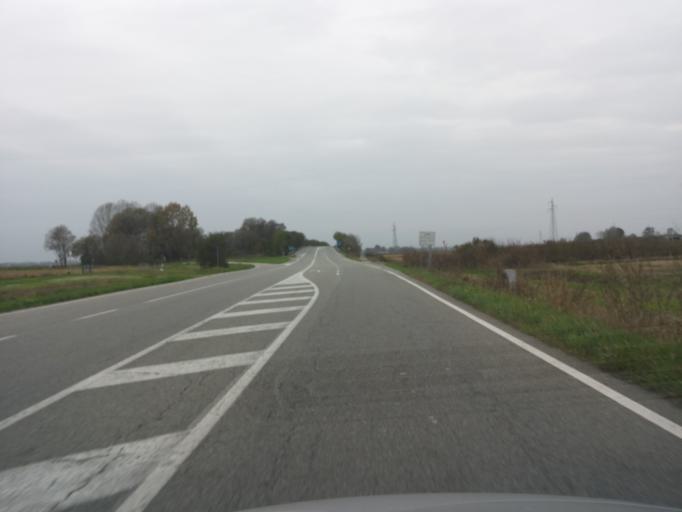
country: IT
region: Piedmont
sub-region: Provincia di Alessandria
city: Morano sul Po
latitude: 45.1750
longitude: 8.3369
